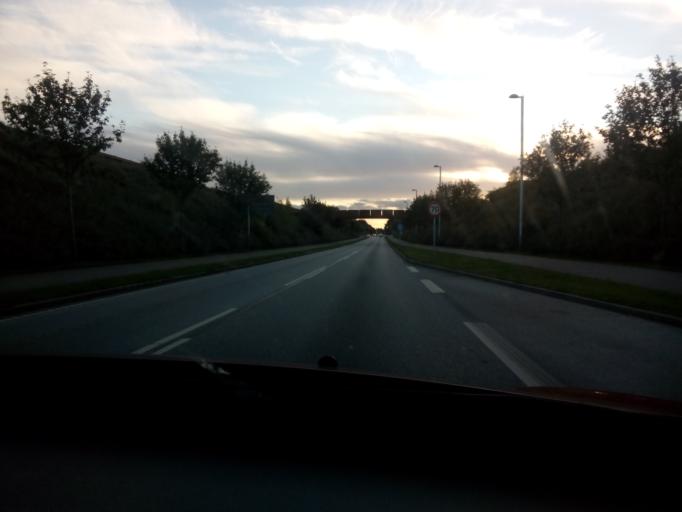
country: DK
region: Central Jutland
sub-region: Randers Kommune
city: Randers
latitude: 56.4818
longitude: 10.0412
